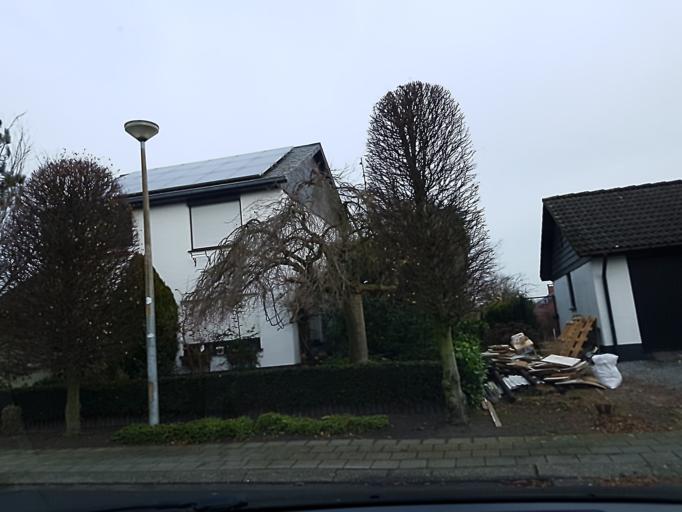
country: BE
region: Flanders
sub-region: Provincie Antwerpen
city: Putte
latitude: 51.0525
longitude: 4.6326
